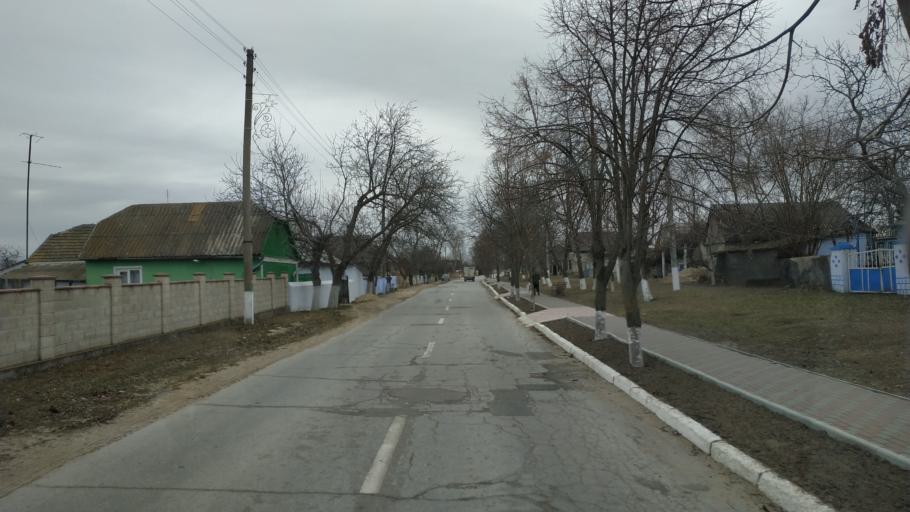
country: MD
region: Telenesti
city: Cocieri
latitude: 47.3431
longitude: 29.0939
